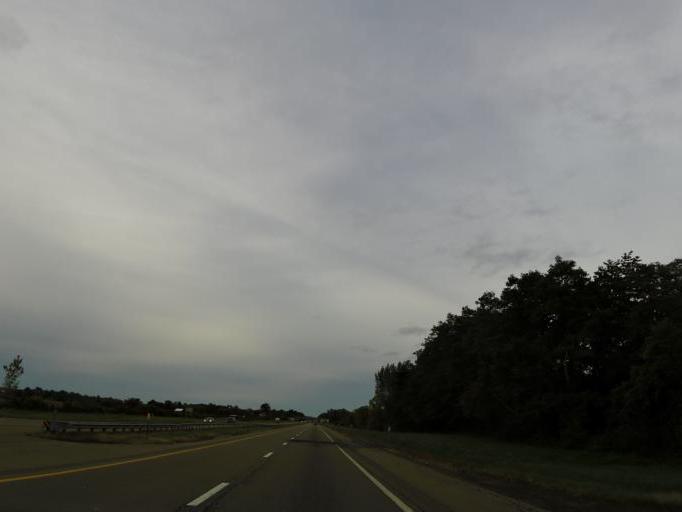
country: US
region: New York
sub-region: Chautauqua County
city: Silver Creek
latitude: 42.5460
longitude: -79.1144
